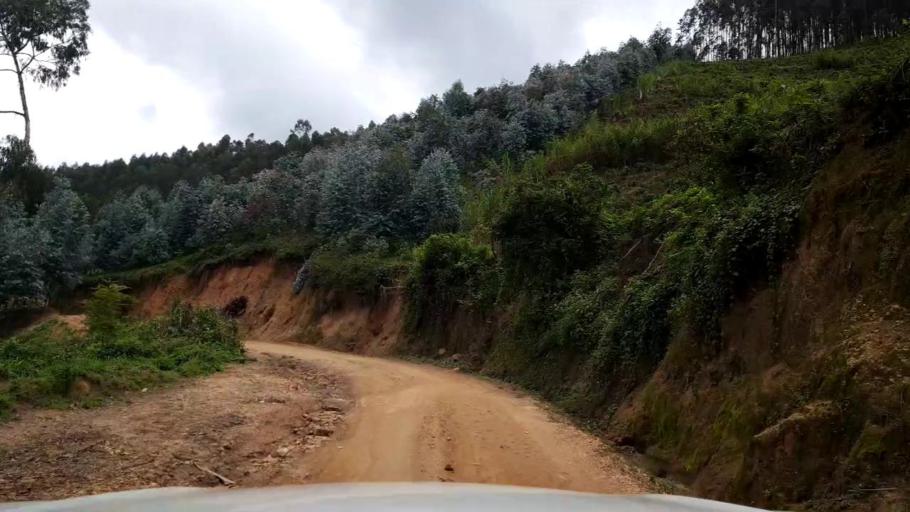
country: RW
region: Western Province
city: Kibuye
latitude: -1.9604
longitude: 29.3955
